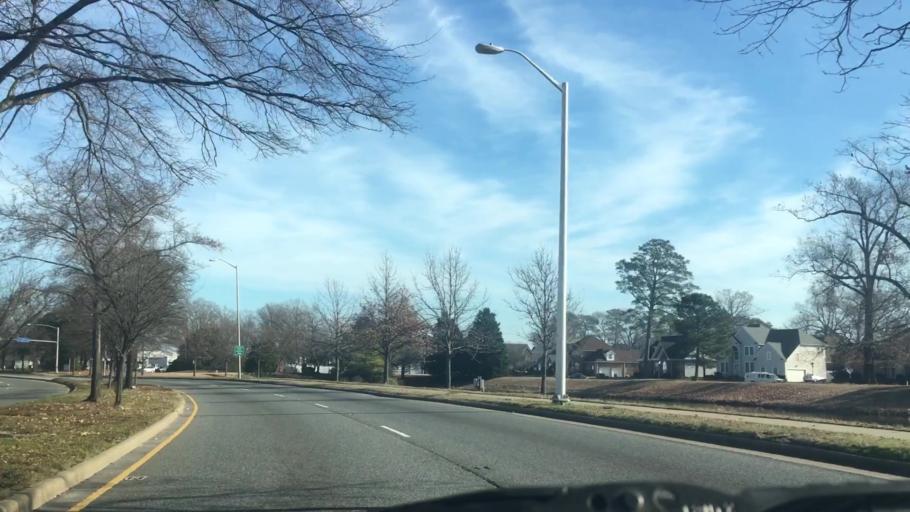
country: US
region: Virginia
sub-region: City of Norfolk
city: Norfolk
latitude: 36.8486
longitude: -76.2499
